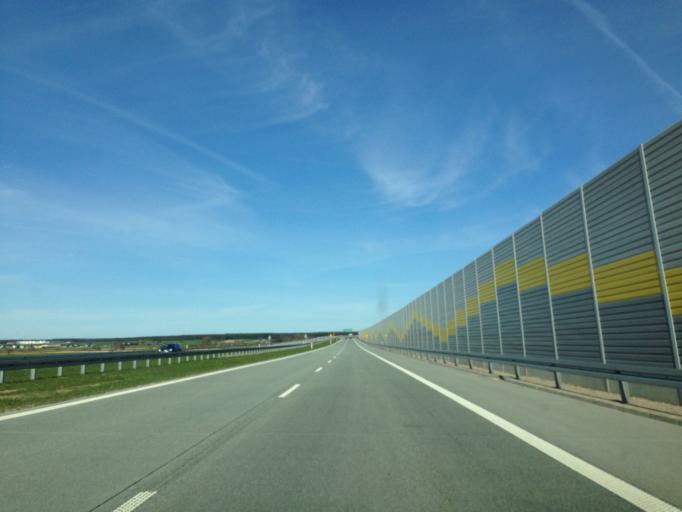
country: PL
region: Lodz Voivodeship
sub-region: Powiat sieradzki
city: Sieradz
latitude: 51.5773
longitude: 18.7945
